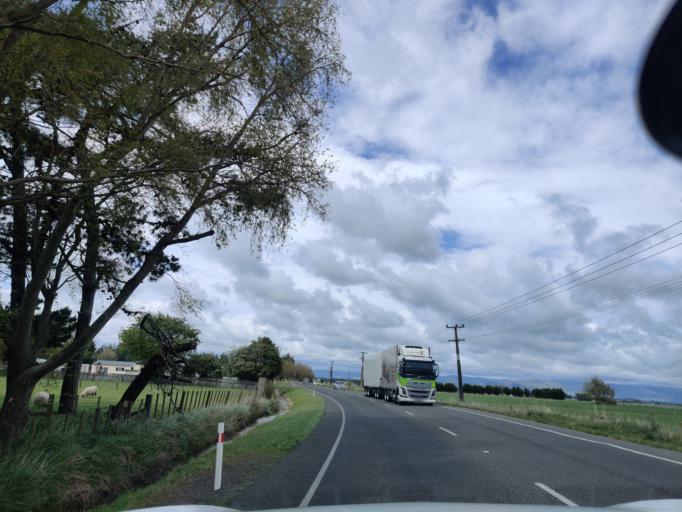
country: NZ
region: Manawatu-Wanganui
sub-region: Palmerston North City
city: Palmerston North
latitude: -40.3278
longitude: 175.5075
